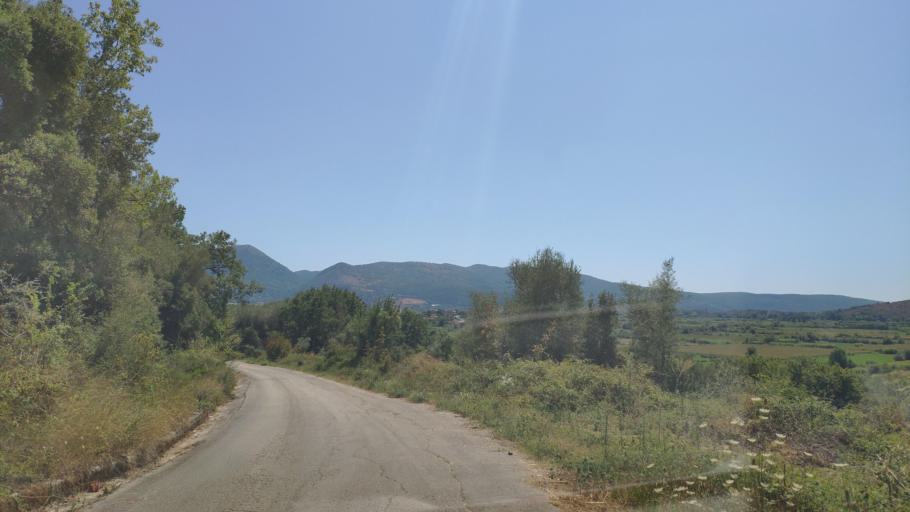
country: GR
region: Epirus
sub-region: Nomos Prevezis
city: Kanalaki
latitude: 39.2700
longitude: 20.6005
